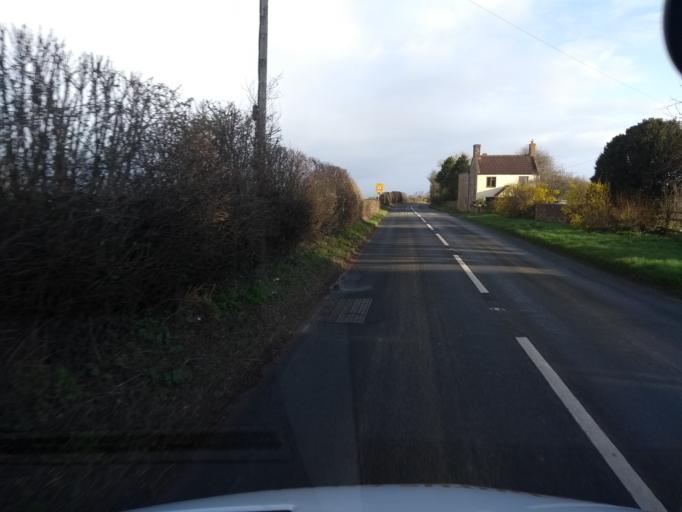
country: GB
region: England
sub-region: Somerset
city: Castle Cary
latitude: 51.0609
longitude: -2.5274
